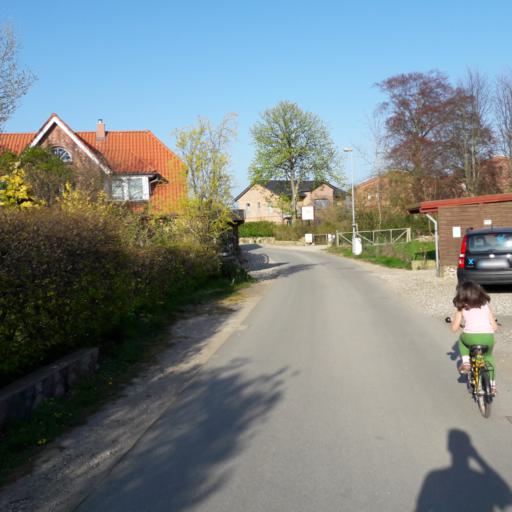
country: DE
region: Schleswig-Holstein
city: Burg auf Fehmarn
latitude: 54.4267
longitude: 11.2268
